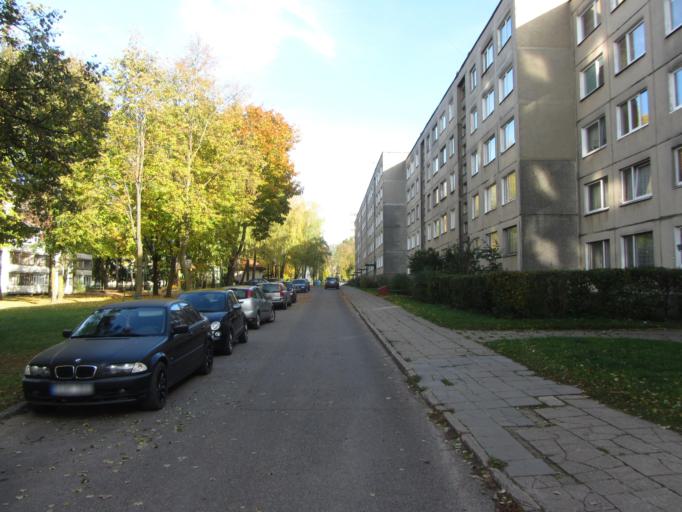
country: LT
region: Vilnius County
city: Elektrenai
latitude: 54.7874
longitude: 24.6591
